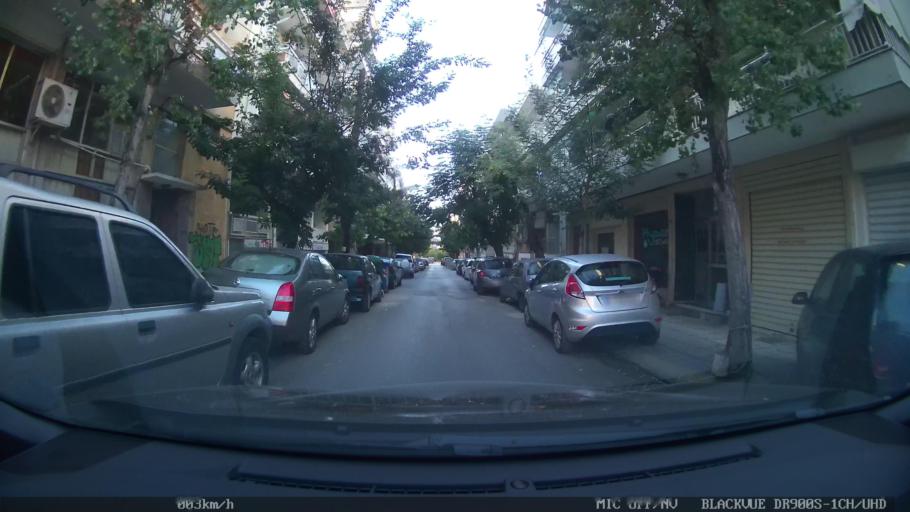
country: GR
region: Central Macedonia
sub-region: Nomos Thessalonikis
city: Triandria
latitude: 40.6159
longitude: 22.9681
